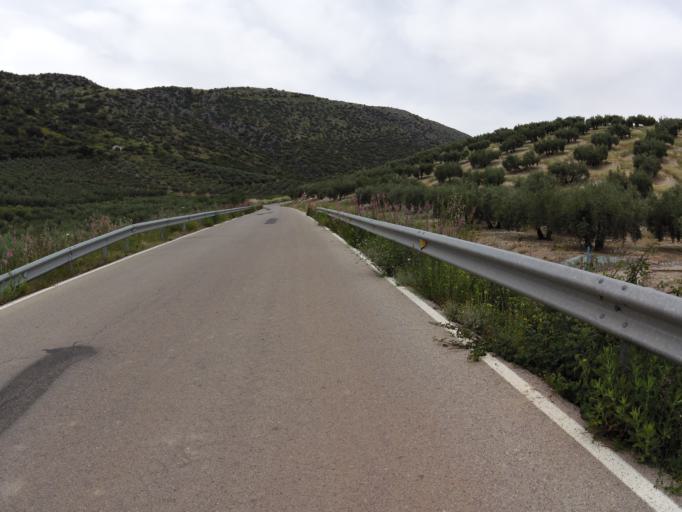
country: ES
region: Andalusia
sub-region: Province of Cordoba
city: Luque
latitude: 37.5188
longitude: -4.2189
